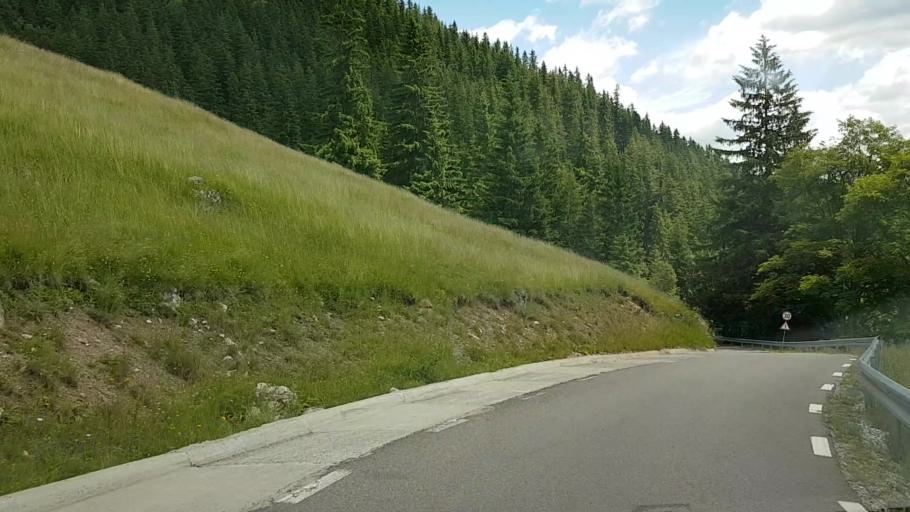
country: RO
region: Suceava
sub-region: Municipiul Campulung Moldovenesc
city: Campulung Moldovenesc
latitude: 47.4368
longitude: 25.5633
